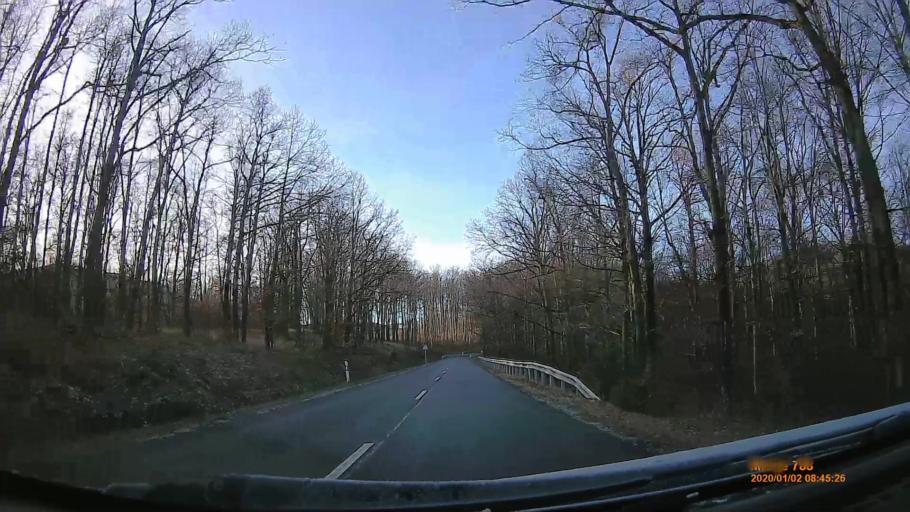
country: HU
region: Heves
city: Paradsasvar
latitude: 47.9018
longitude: 19.9886
